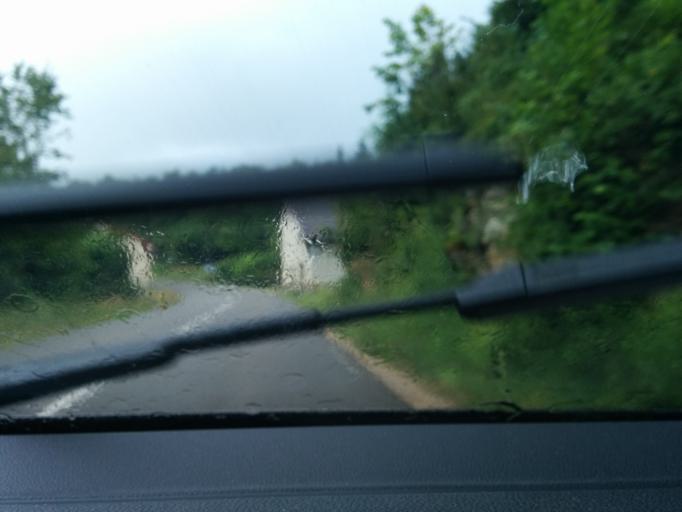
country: FR
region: Franche-Comte
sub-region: Departement du Jura
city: Saint-Lupicin
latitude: 46.4164
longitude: 5.7976
